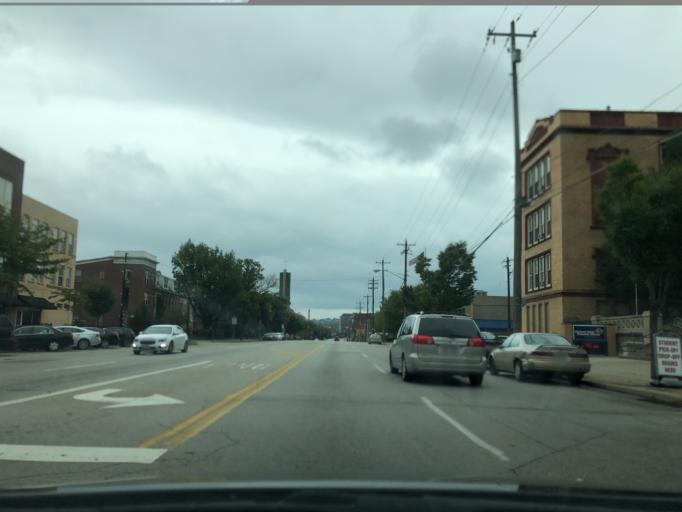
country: US
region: Kentucky
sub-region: Kenton County
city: Ludlow
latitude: 39.1113
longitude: -84.5276
